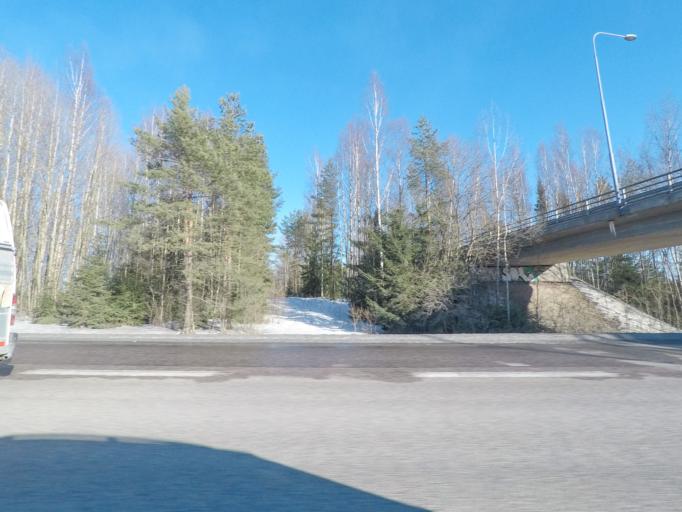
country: FI
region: Uusimaa
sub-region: Helsinki
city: Kerava
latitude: 60.3604
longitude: 25.1149
